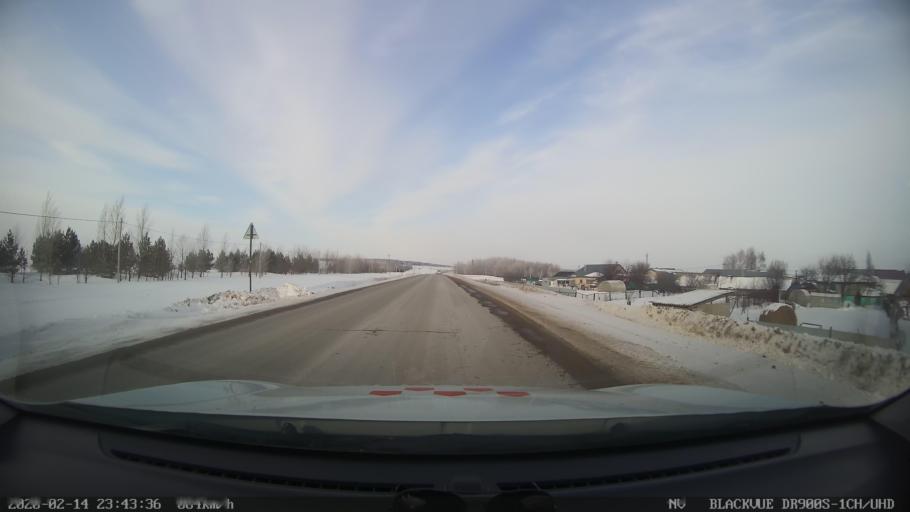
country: RU
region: Tatarstan
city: Kuybyshevskiy Zaton
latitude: 55.2037
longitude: 49.2493
